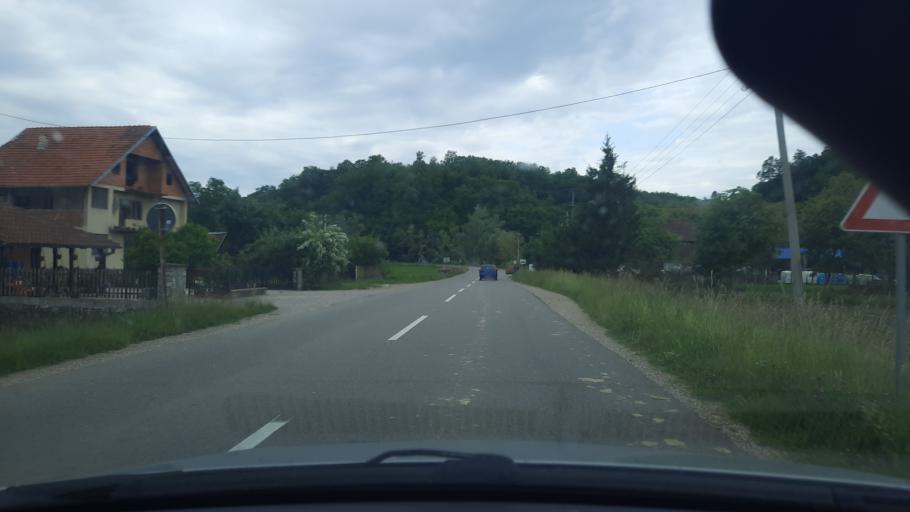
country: RS
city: Jarebice
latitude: 44.5001
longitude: 19.4882
